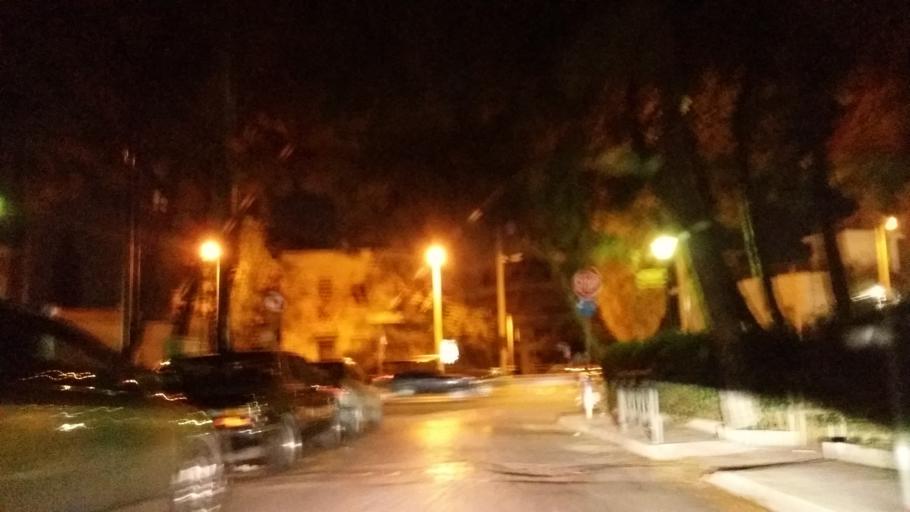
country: GR
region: Attica
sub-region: Nomarchia Athinas
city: Khalandrion
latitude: 38.0201
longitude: 23.7946
